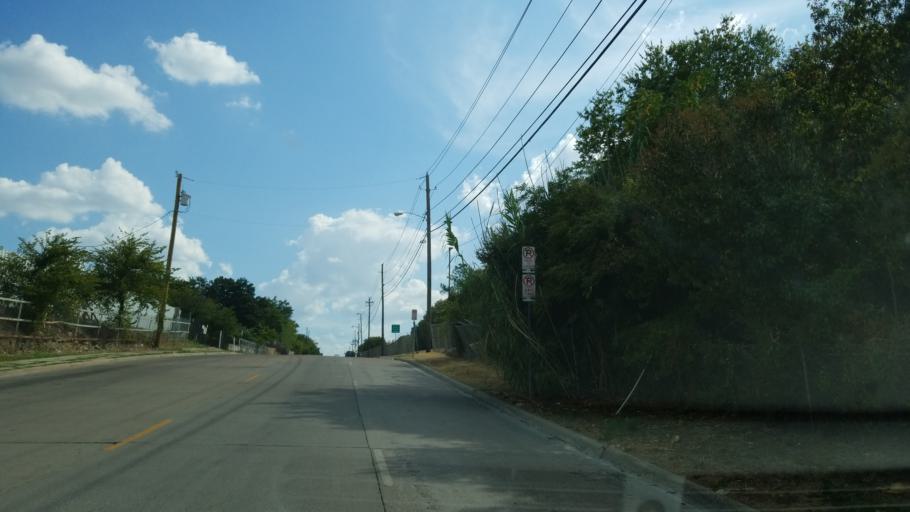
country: US
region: Texas
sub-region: Dallas County
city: Dallas
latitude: 32.7714
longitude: -96.8480
